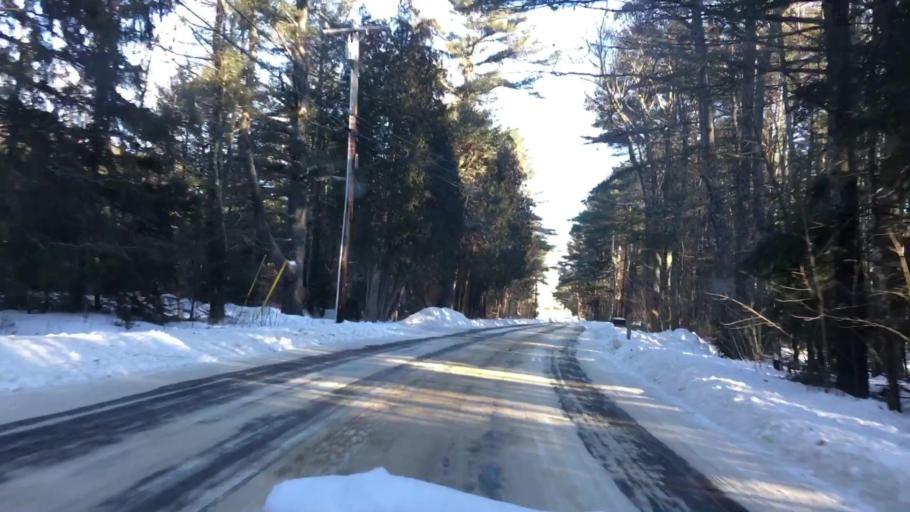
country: US
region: Maine
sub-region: Cumberland County
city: Brunswick
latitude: 43.9522
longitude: -69.9303
